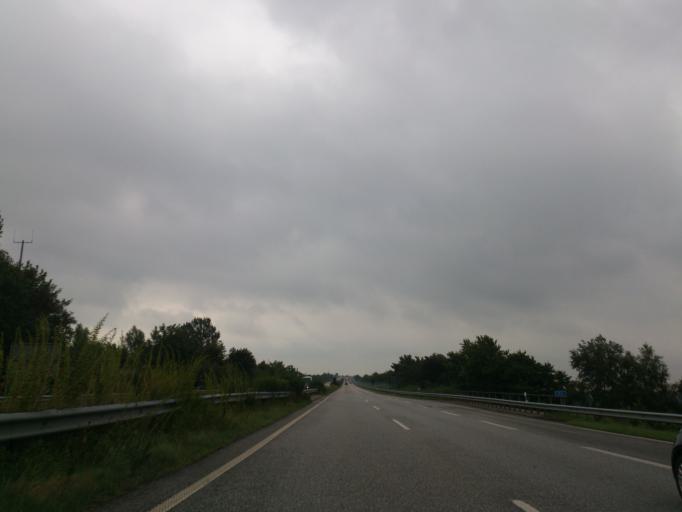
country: DE
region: Schleswig-Holstein
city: Schafstedt
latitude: 54.0743
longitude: 9.2876
